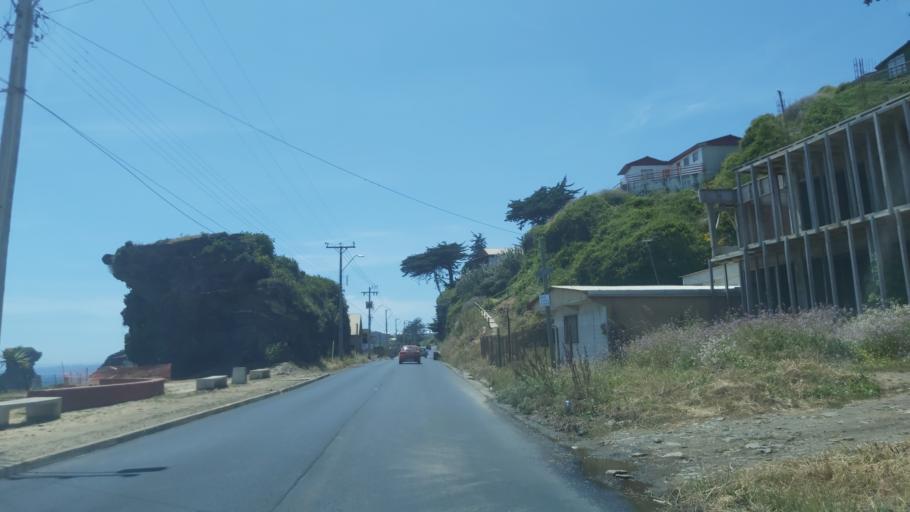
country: CL
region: Maule
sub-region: Provincia de Cauquenes
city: Cauquenes
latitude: -35.8211
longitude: -72.5987
